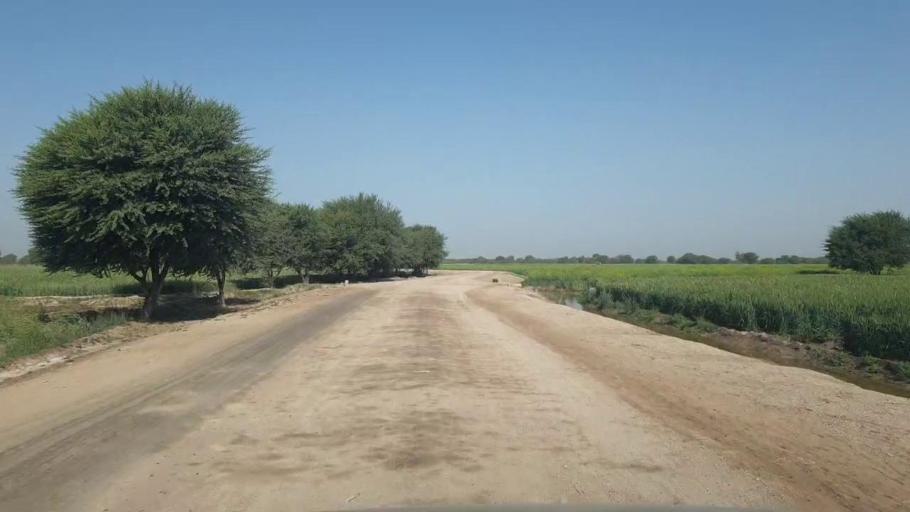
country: PK
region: Sindh
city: Umarkot
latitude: 25.2945
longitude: 69.6583
